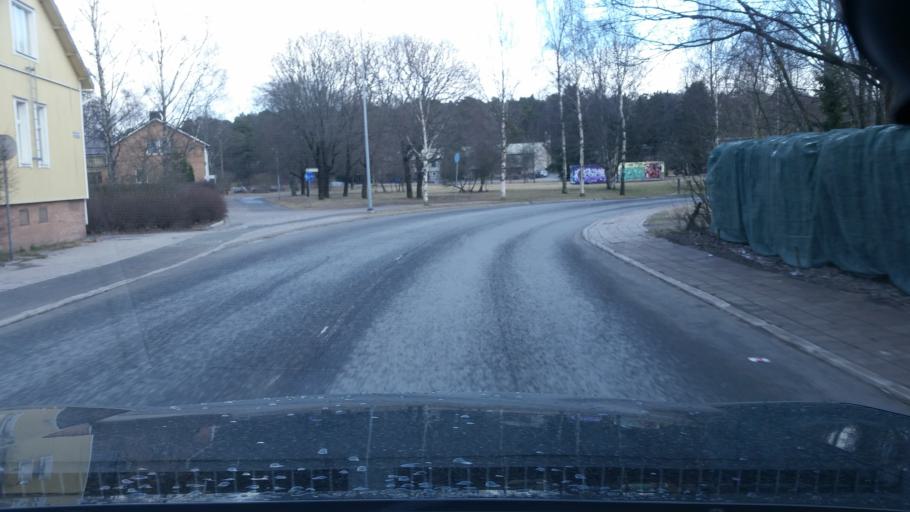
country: FI
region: Varsinais-Suomi
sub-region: Turku
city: Turku
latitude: 60.4371
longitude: 22.2617
